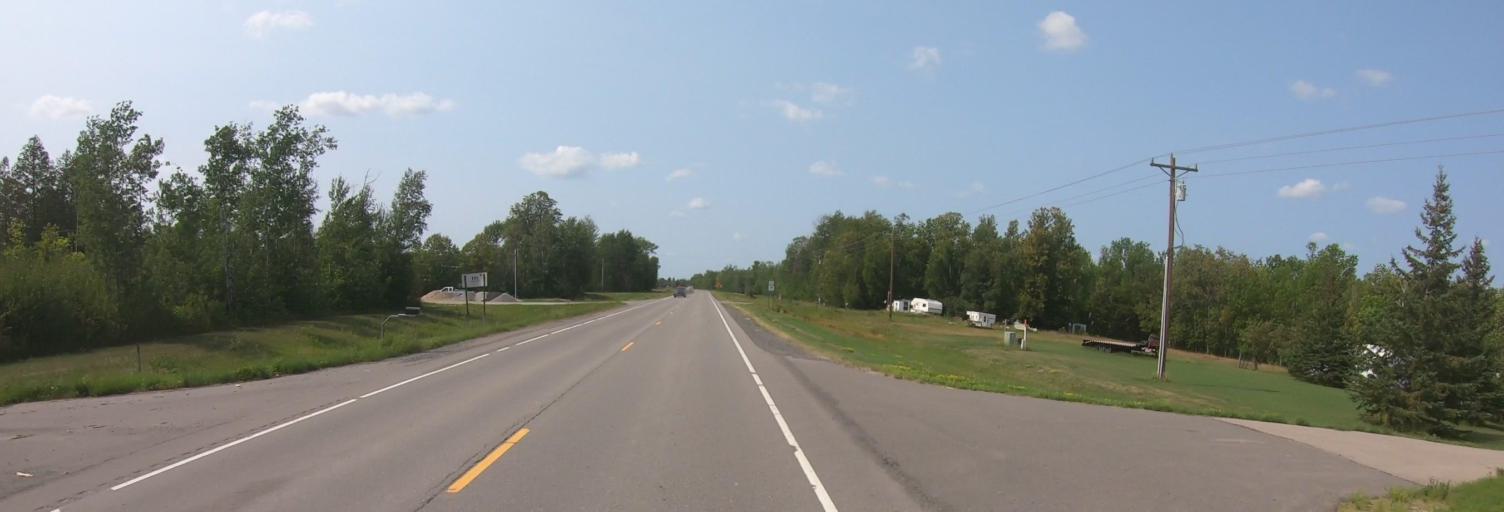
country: US
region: Minnesota
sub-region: Lake of the Woods County
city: Baudette
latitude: 48.6935
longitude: -94.4690
